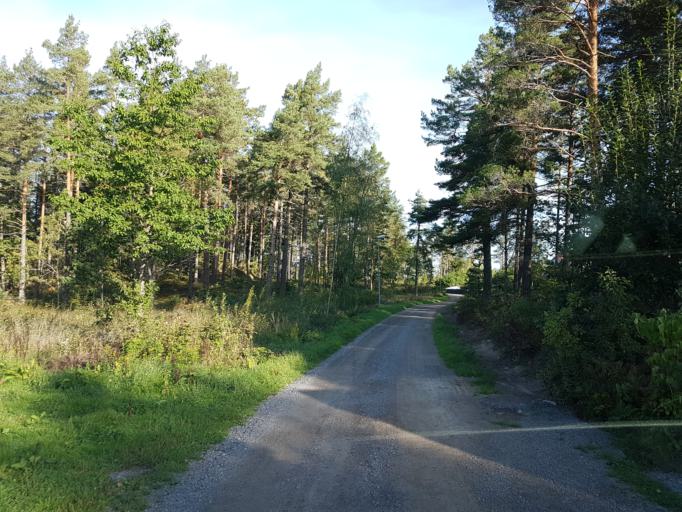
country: SE
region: OEstergoetland
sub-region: Atvidabergs Kommun
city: Atvidaberg
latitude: 58.2201
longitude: 16.0218
